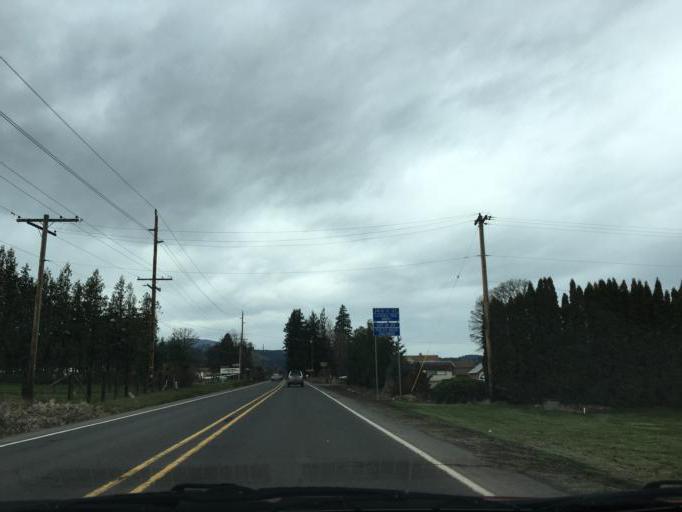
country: US
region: Oregon
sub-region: Hood River County
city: Hood River
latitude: 45.6787
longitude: -121.5381
